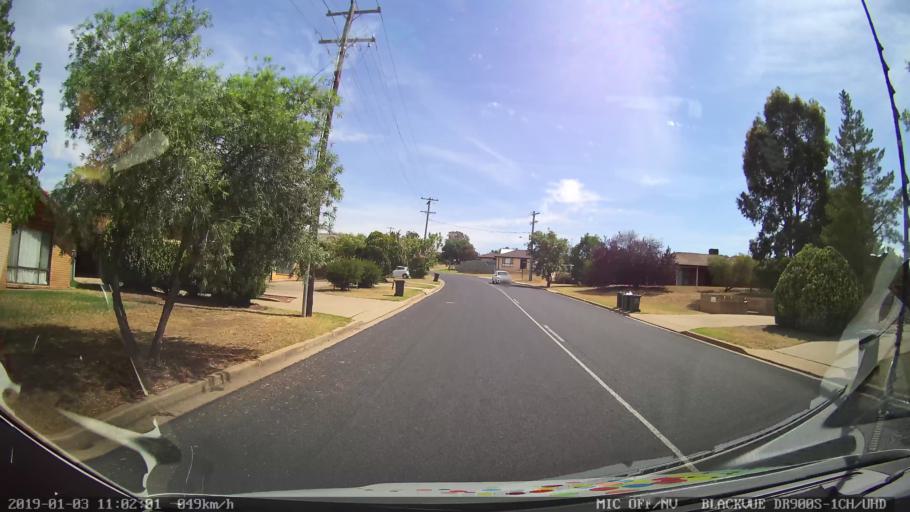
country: AU
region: New South Wales
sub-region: Young
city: Young
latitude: -34.3009
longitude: 148.2992
